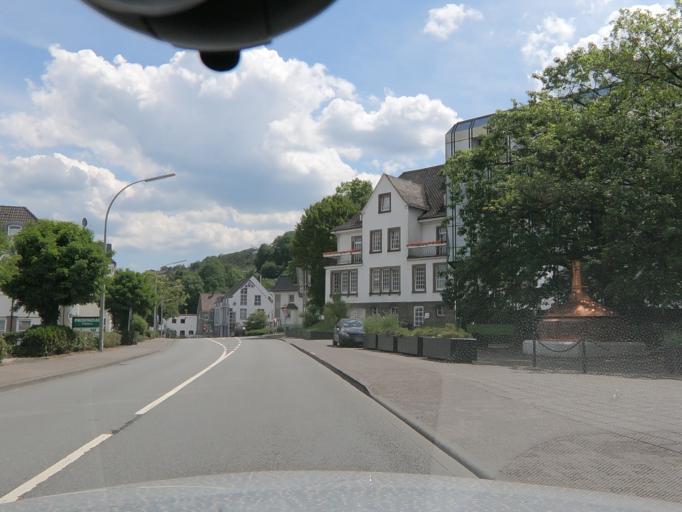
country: DE
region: North Rhine-Westphalia
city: Warstein
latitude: 51.4420
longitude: 8.3512
